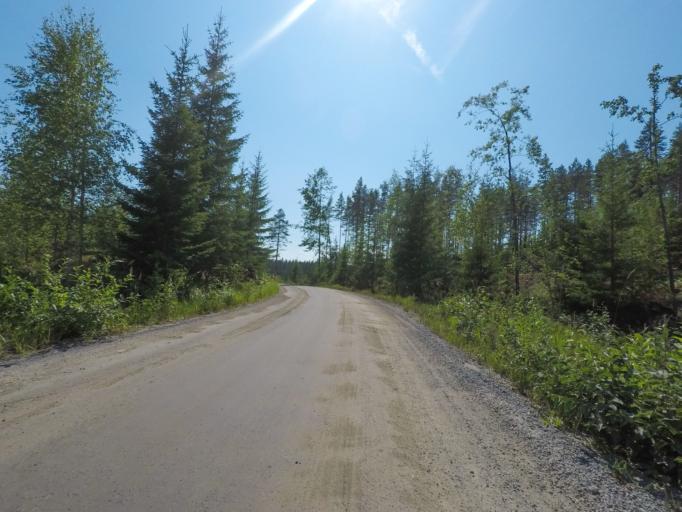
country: FI
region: Southern Savonia
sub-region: Mikkeli
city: Puumala
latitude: 61.4077
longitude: 28.0463
